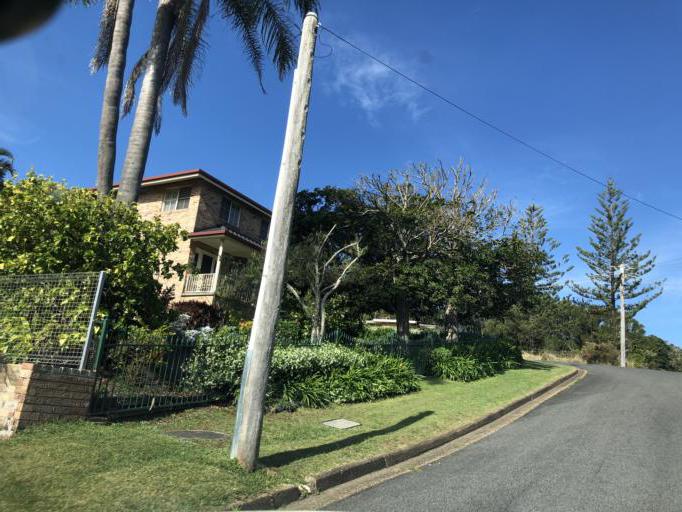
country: AU
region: New South Wales
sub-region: Coffs Harbour
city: Moonee Beach
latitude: -30.2347
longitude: 153.1508
